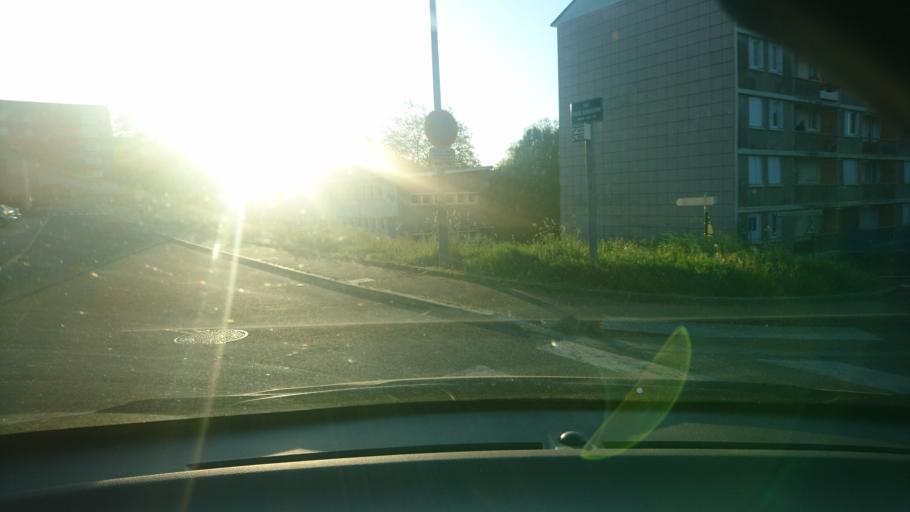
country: FR
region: Limousin
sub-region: Departement de la Haute-Vienne
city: Limoges
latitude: 45.8544
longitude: 1.2682
